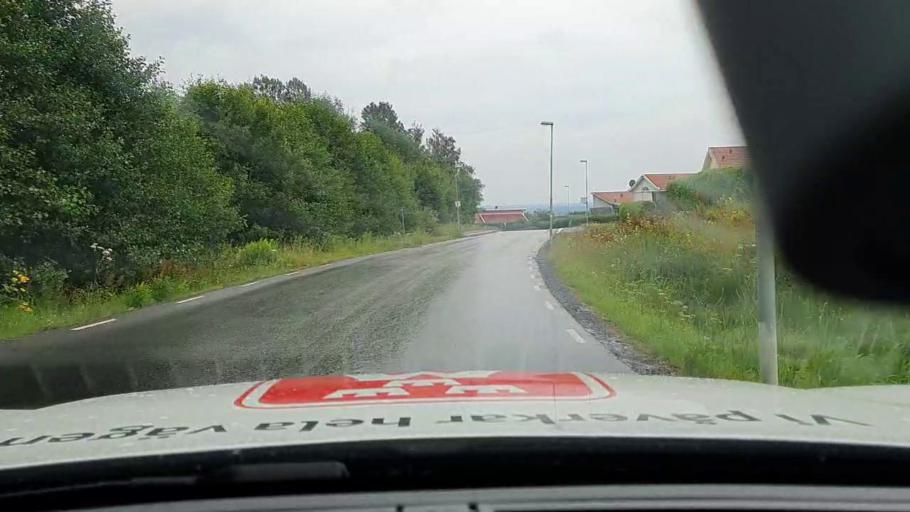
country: SE
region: Vaestra Goetaland
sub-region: Skovde Kommun
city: Skoevde
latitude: 58.4172
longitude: 13.8235
